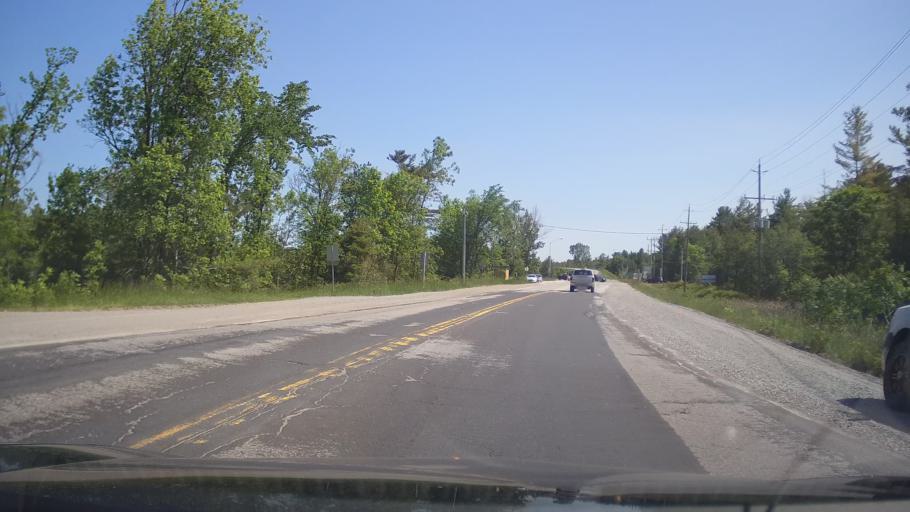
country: CA
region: Ontario
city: Orillia
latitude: 44.7519
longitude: -79.3386
